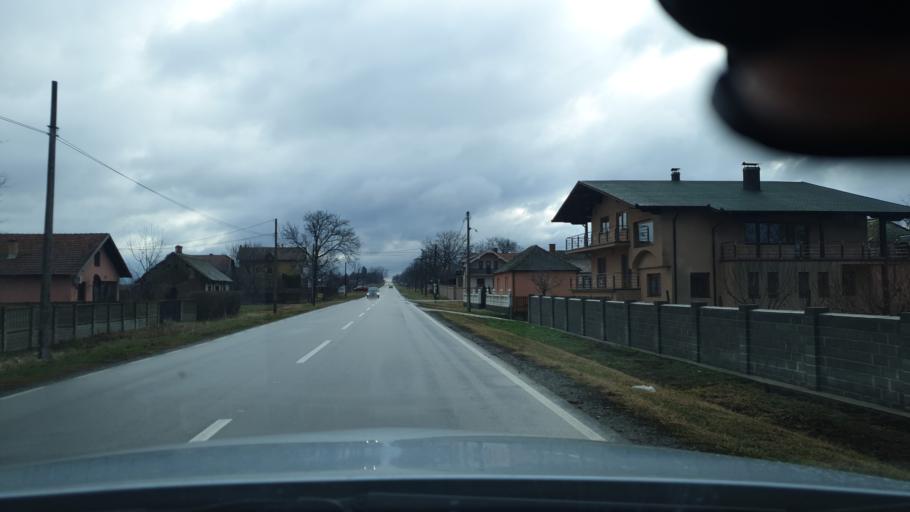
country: RS
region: Central Serbia
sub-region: Branicevski Okrug
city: Malo Crnice
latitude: 44.5754
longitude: 21.2870
